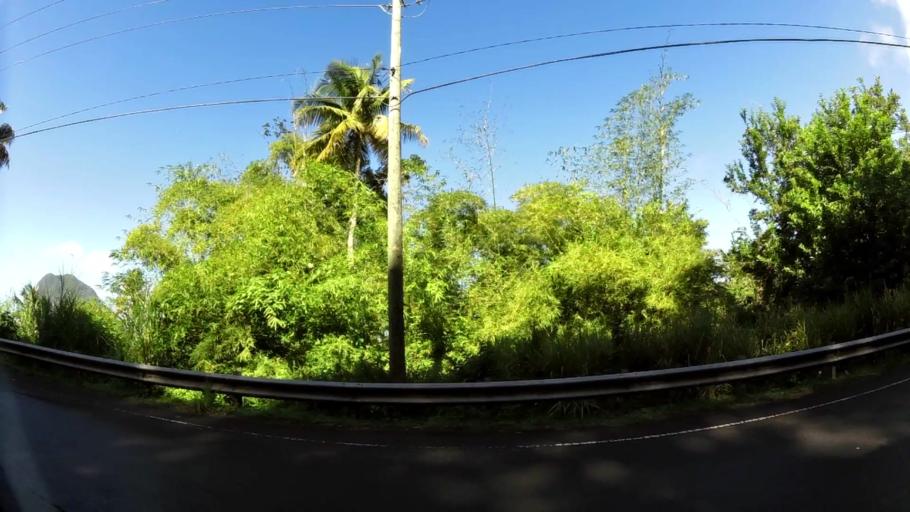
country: LC
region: Choiseul Quarter
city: Choiseul
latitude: 13.8144
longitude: -61.0398
